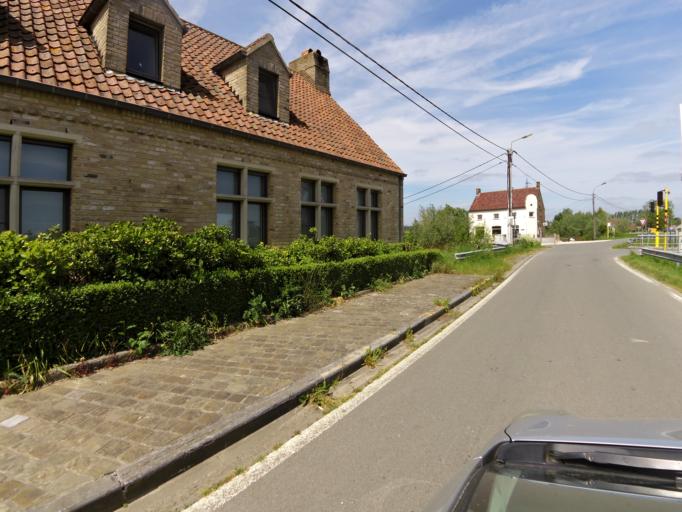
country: BE
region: Flanders
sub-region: Provincie West-Vlaanderen
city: Diksmuide
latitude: 50.9813
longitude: 2.8056
